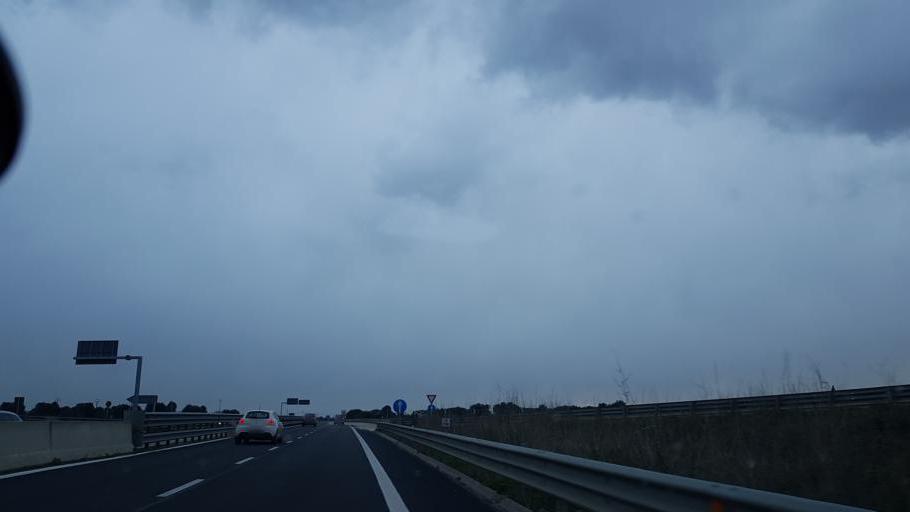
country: IT
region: Apulia
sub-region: Provincia di Brindisi
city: Mesagne
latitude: 40.5908
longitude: 17.8592
